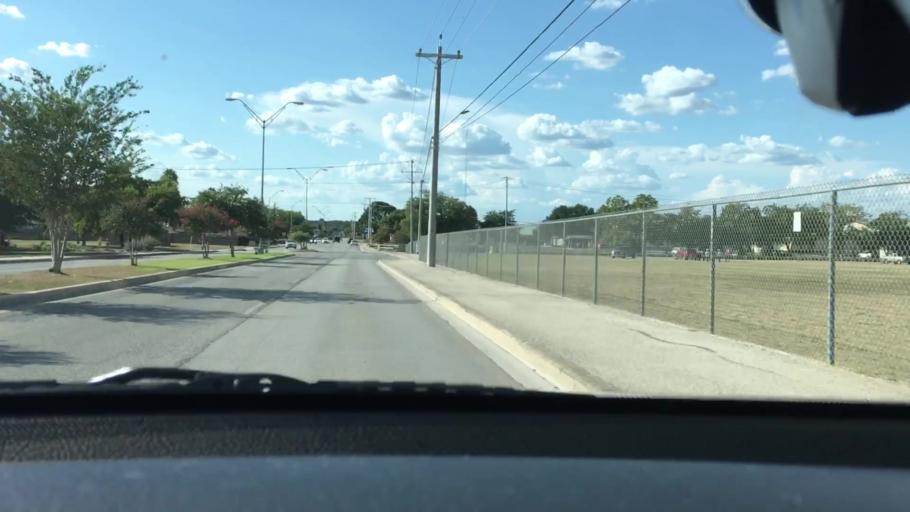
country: US
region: Texas
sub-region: Guadalupe County
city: Schertz
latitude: 29.5622
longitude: -98.2682
